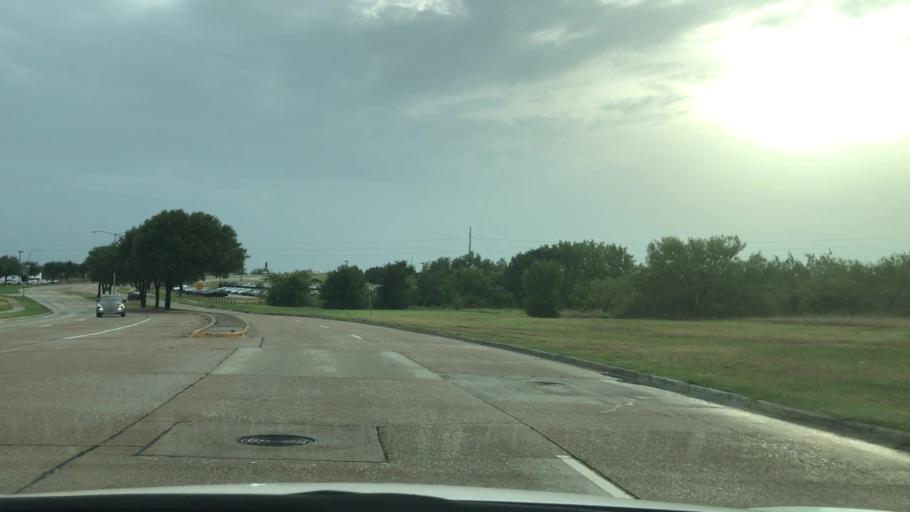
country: US
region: Texas
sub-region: Denton County
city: Lewisville
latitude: 33.0577
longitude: -97.0058
